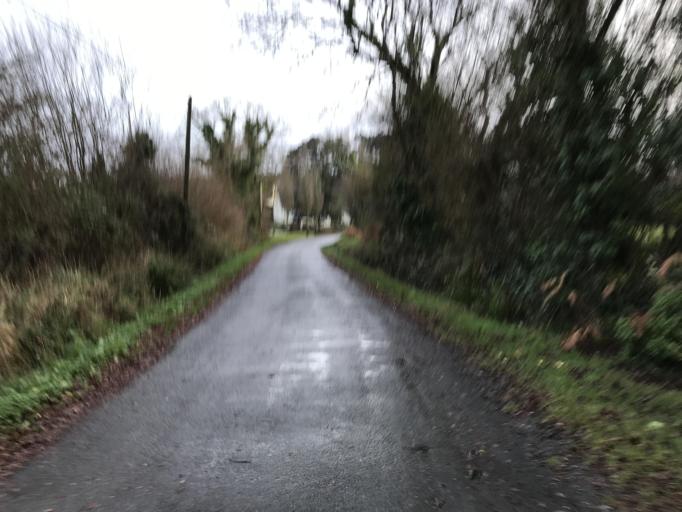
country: FR
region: Brittany
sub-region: Departement du Finistere
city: Logonna-Daoulas
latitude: 48.3222
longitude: -4.3119
